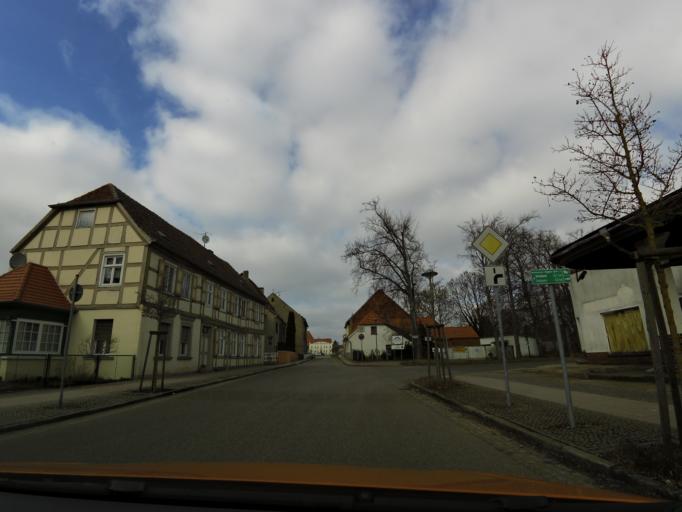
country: DE
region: Brandenburg
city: Wusterhausen
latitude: 52.8876
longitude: 12.4615
